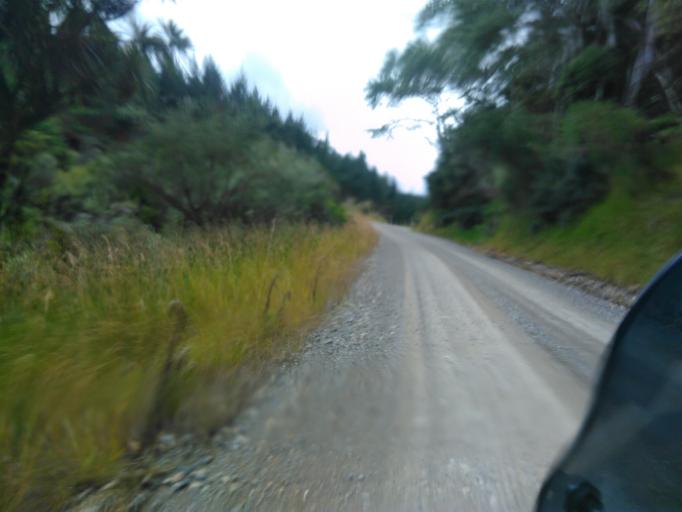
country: NZ
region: Gisborne
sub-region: Gisborne District
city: Gisborne
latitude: -38.0534
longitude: 178.1307
